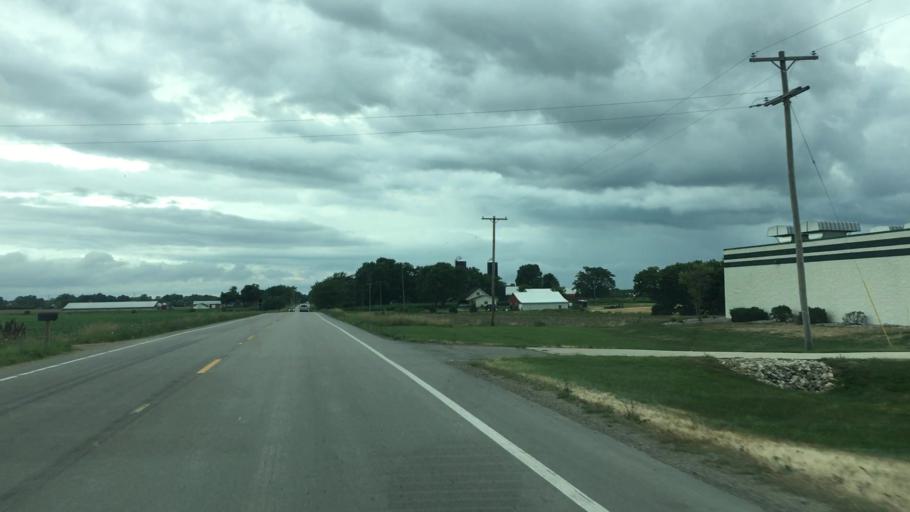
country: US
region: Michigan
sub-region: Ottawa County
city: Zeeland
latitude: 42.7828
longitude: -85.9211
